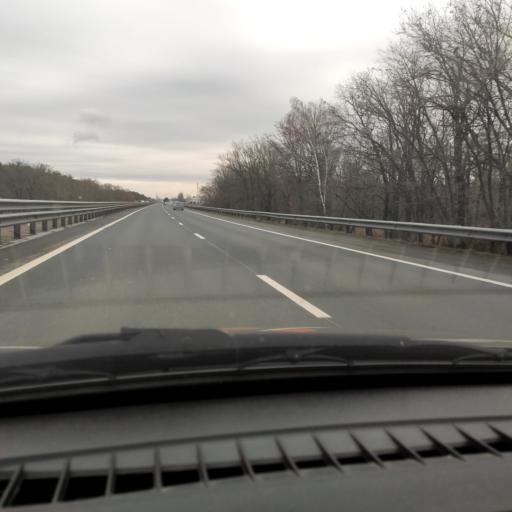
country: RU
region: Samara
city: Zhigulevsk
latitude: 53.5130
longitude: 49.5813
